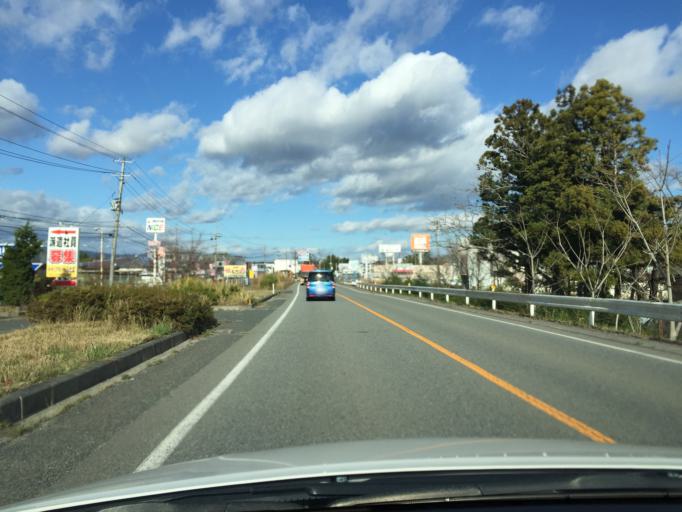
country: JP
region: Fukushima
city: Namie
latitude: 37.4818
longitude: 141.0065
